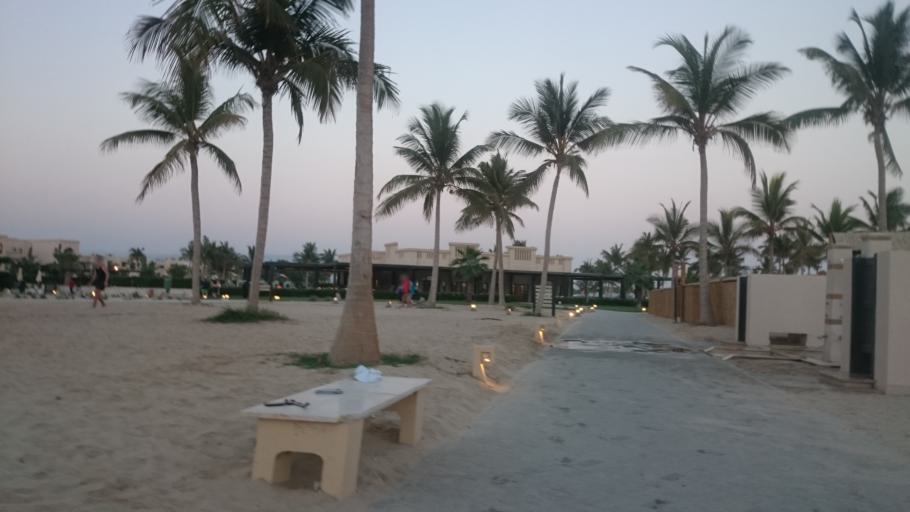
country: OM
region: Zufar
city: Salalah
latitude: 17.0290
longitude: 54.2975
